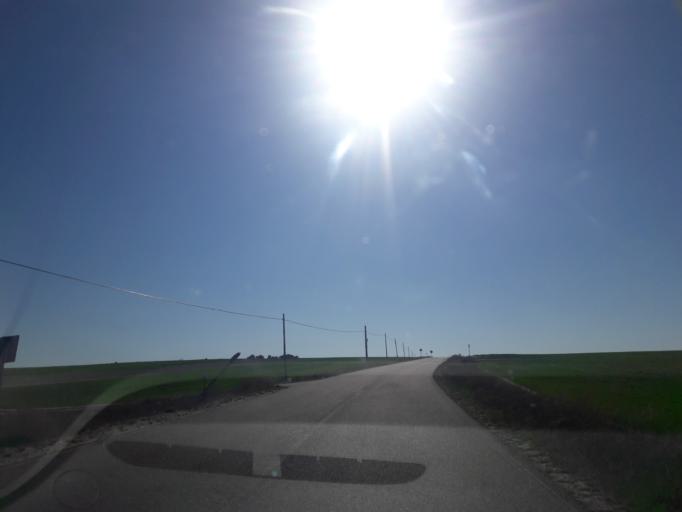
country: ES
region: Castille and Leon
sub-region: Provincia de Salamanca
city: Tordillos
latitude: 40.8485
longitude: -5.3184
